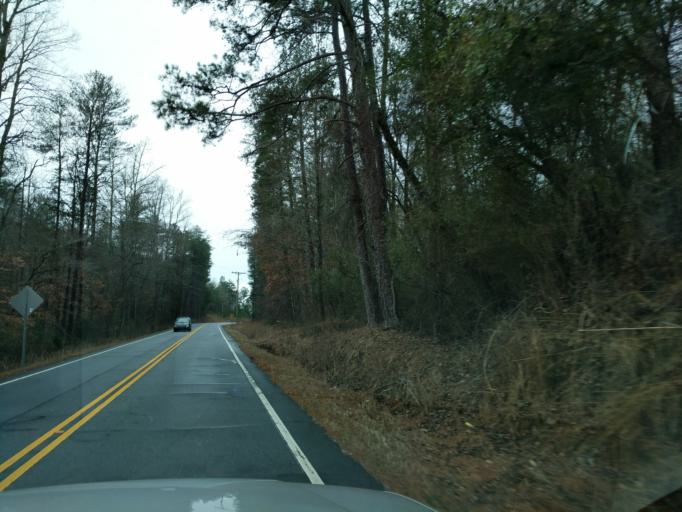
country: US
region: South Carolina
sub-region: Oconee County
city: Walhalla
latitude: 34.8123
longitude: -83.0493
